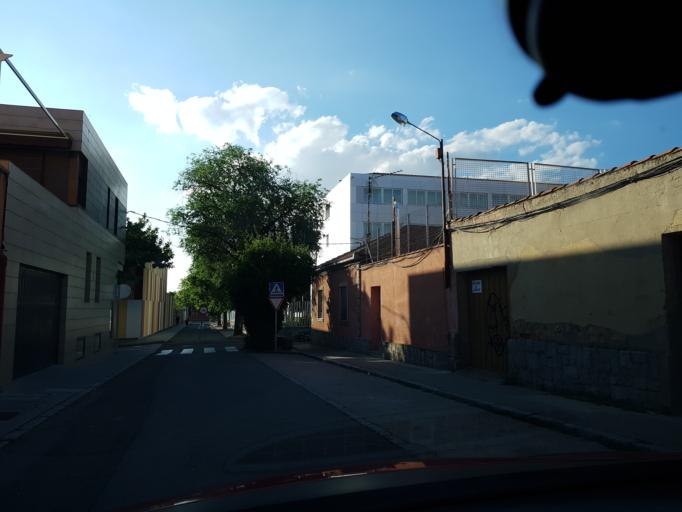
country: ES
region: Castille and Leon
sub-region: Provincia de Segovia
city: Segovia
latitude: 40.9438
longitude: -4.1052
